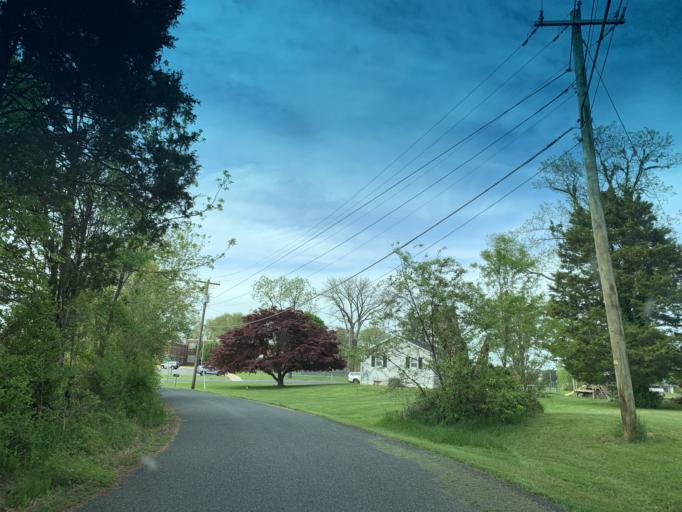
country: US
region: Maryland
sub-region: Harford County
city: South Bel Air
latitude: 39.6470
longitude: -76.2658
